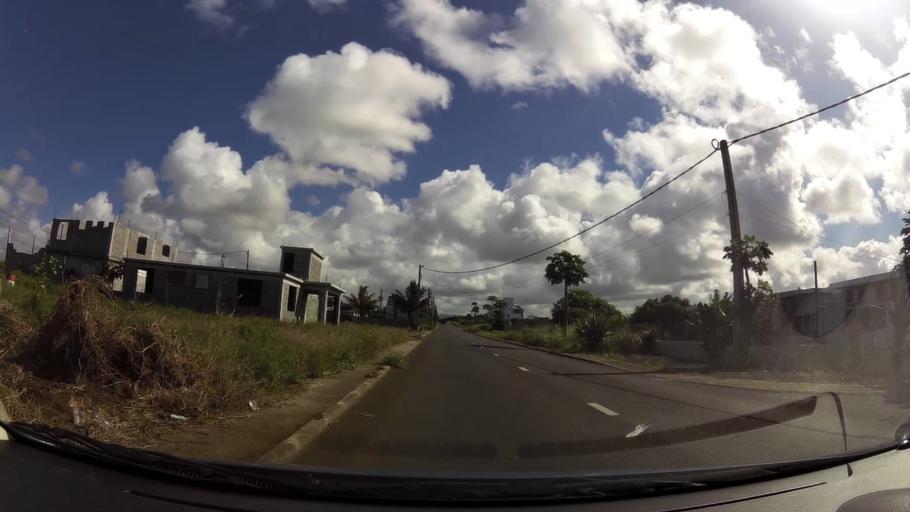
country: MU
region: Grand Port
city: Plaine Magnien
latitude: -20.4364
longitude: 57.6660
